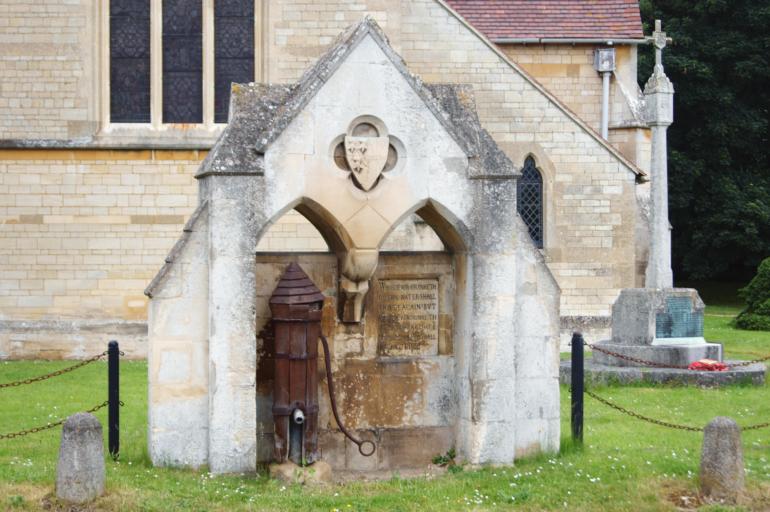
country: GB
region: England
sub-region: Cambridgeshire
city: Gamlingay
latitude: 52.1750
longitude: -0.1736
